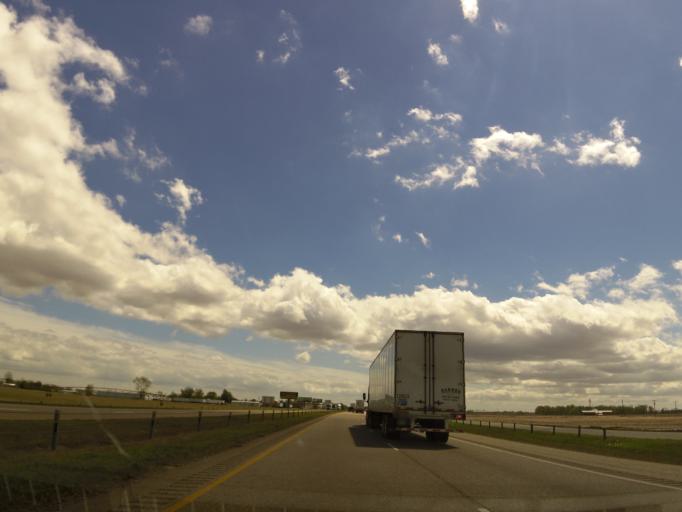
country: US
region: Arkansas
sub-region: Crittenden County
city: Marion
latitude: 35.2433
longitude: -90.2179
